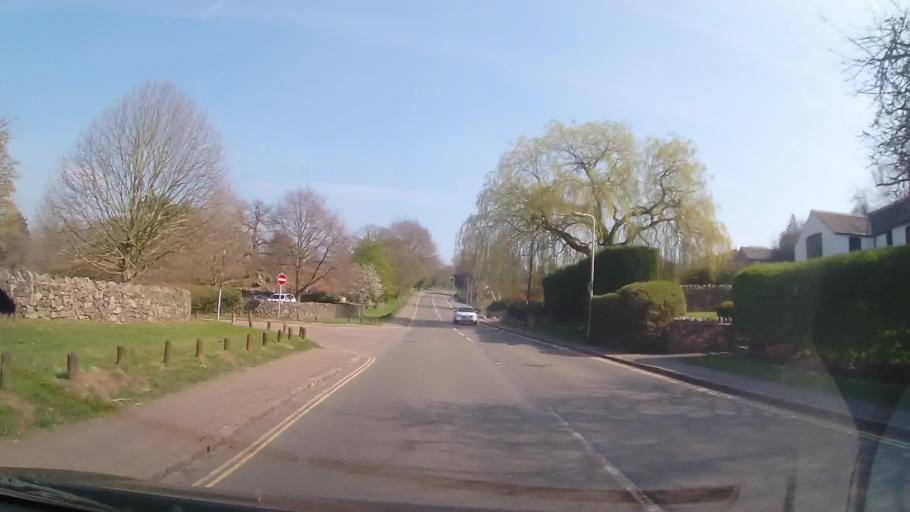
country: GB
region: England
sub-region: Leicestershire
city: Anstey
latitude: 52.6824
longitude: -1.2261
